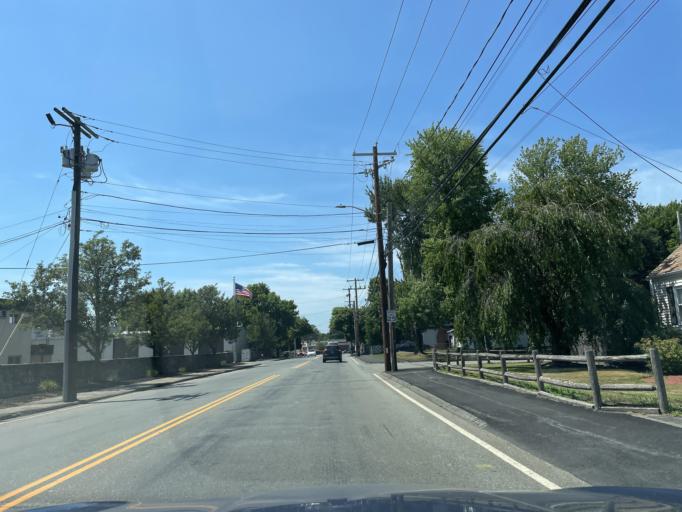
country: US
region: Massachusetts
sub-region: Norfolk County
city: Stoughton
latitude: 42.1349
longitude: -71.0990
